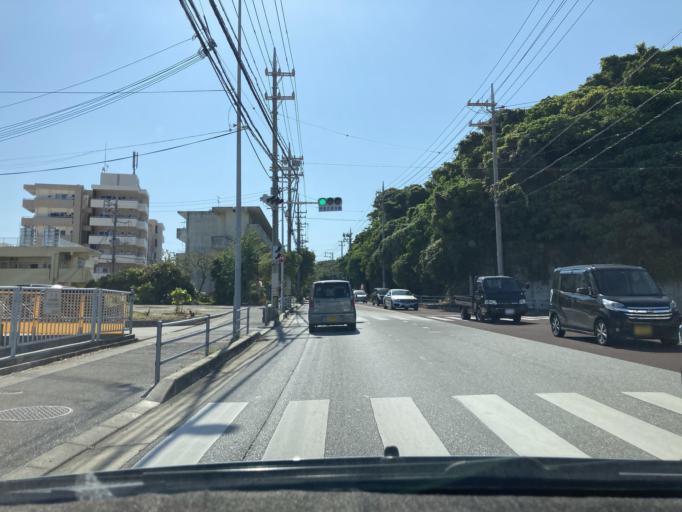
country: JP
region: Okinawa
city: Ginowan
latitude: 26.2604
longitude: 127.7227
